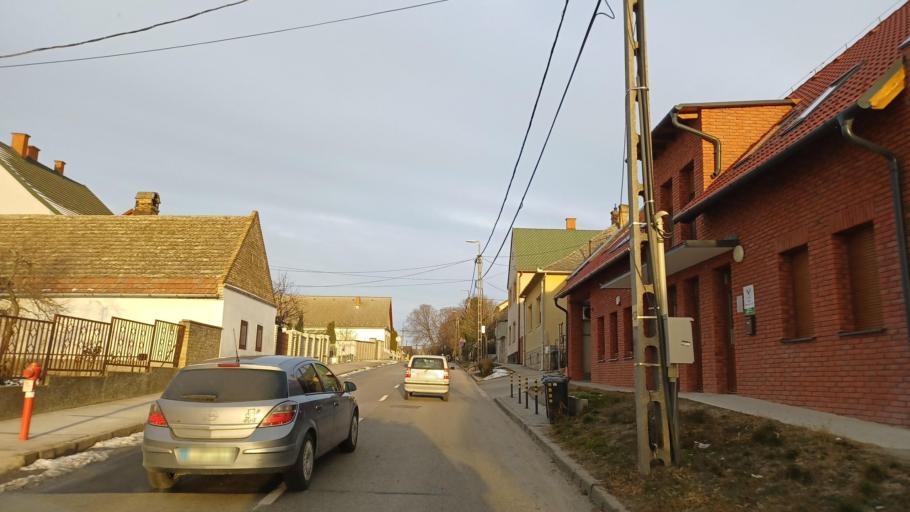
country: HU
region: Tolna
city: Paks
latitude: 46.6268
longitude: 18.8601
